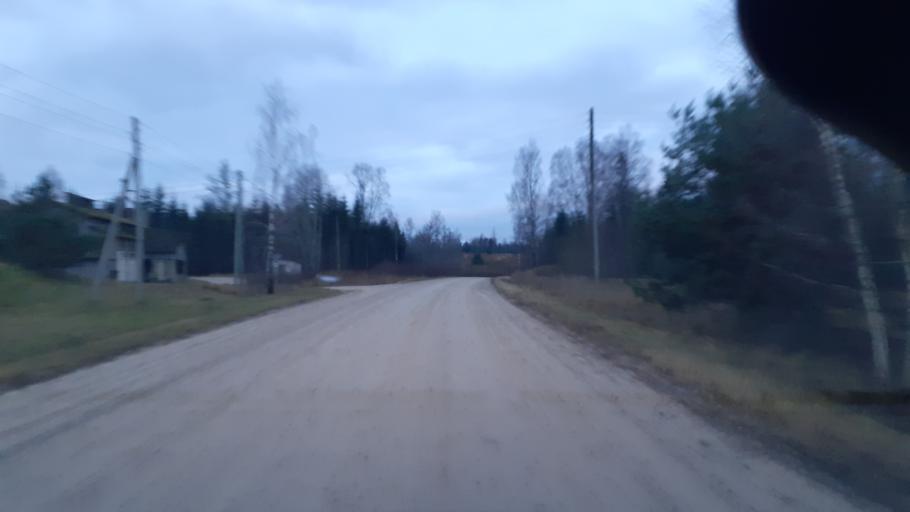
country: LV
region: Kuldigas Rajons
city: Kuldiga
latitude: 56.9505
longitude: 21.7847
